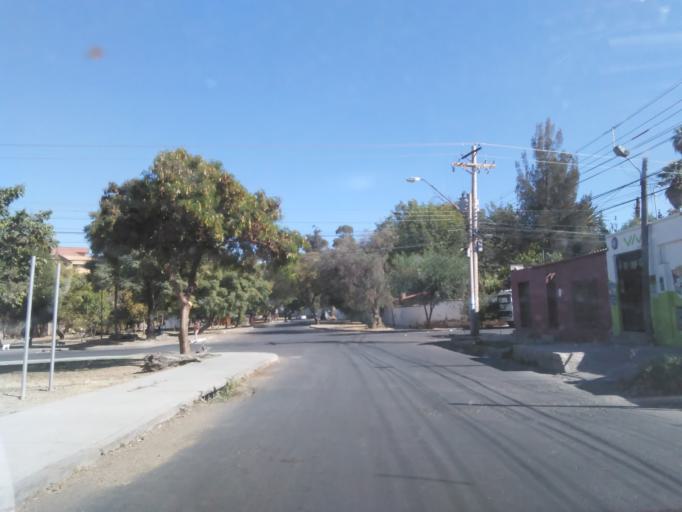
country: BO
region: Cochabamba
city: Cochabamba
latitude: -17.3702
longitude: -66.1531
